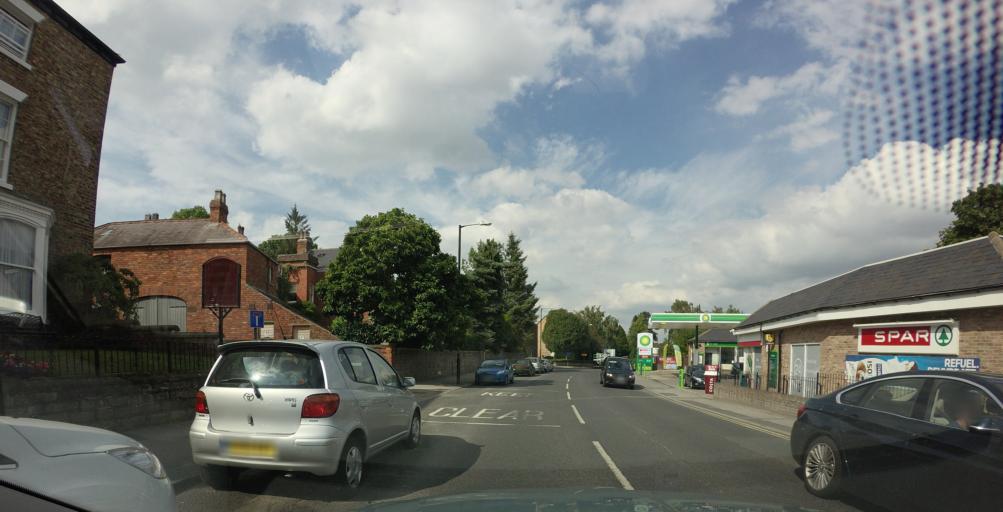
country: GB
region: England
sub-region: North Yorkshire
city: Ripon
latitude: 54.1399
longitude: -1.5242
